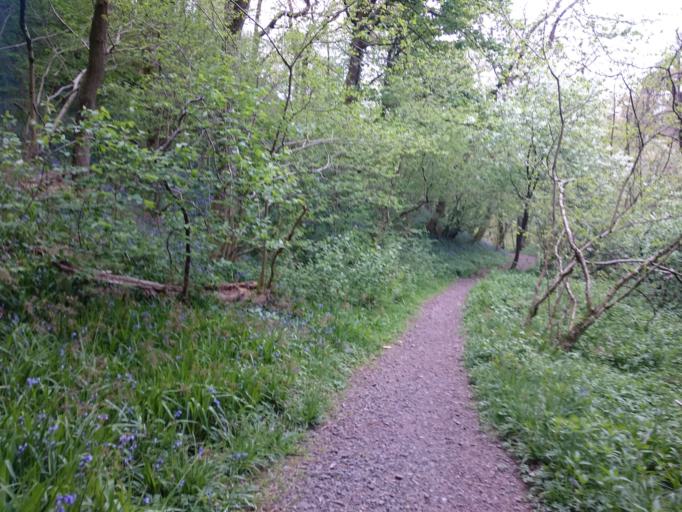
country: GB
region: Scotland
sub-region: Falkirk
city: Dunipace
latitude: 56.0274
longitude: -3.9481
